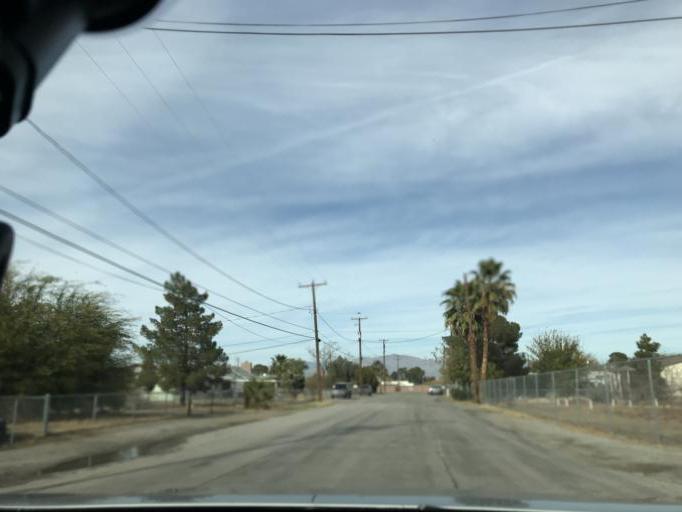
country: US
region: Nevada
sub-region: Clark County
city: Las Vegas
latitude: 36.1792
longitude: -115.1671
